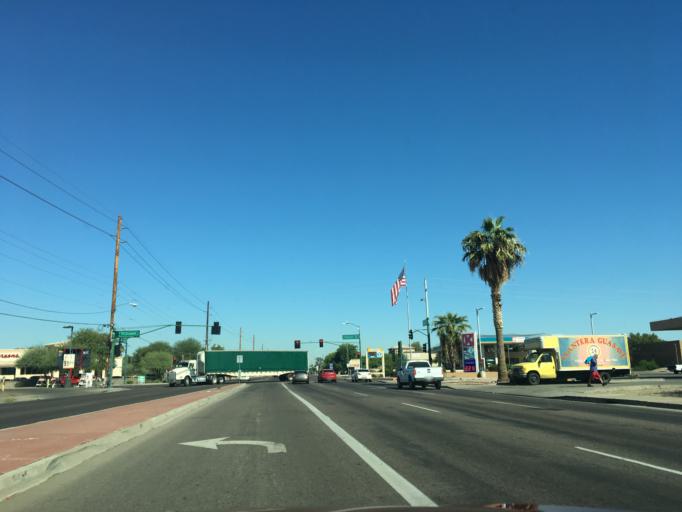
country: US
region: Arizona
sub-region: Maricopa County
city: Glendale
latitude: 33.4651
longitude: -112.1864
